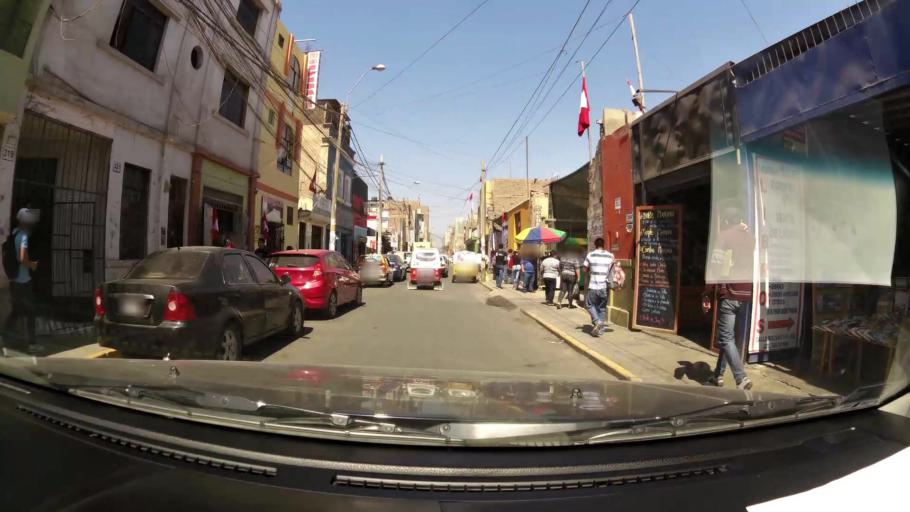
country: PE
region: Ica
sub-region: Provincia de Ica
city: Ica
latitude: -14.0658
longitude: -75.7290
